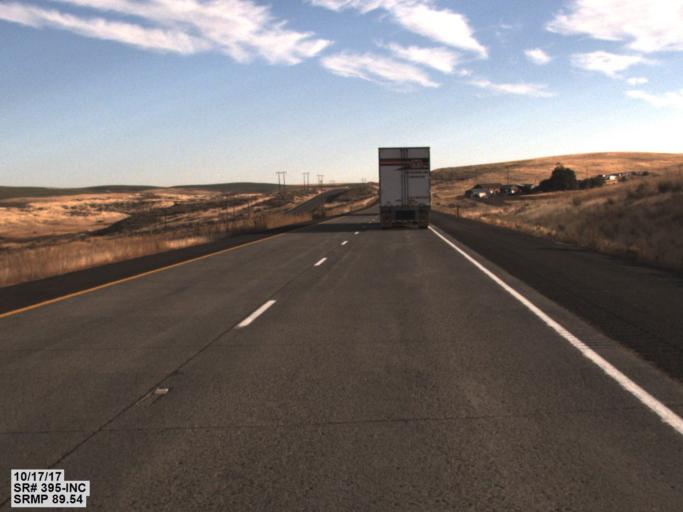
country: US
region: Washington
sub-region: Adams County
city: Ritzville
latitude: 47.0384
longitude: -118.4540
